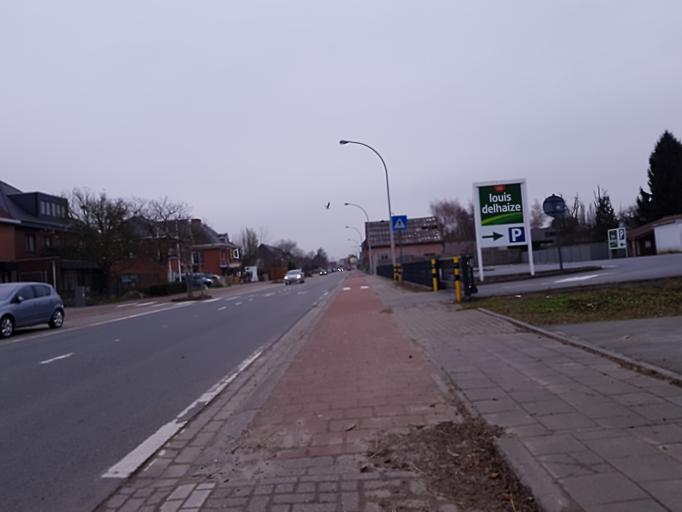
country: BE
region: Flanders
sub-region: Provincie Antwerpen
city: Willebroek
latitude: 51.0491
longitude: 4.3749
